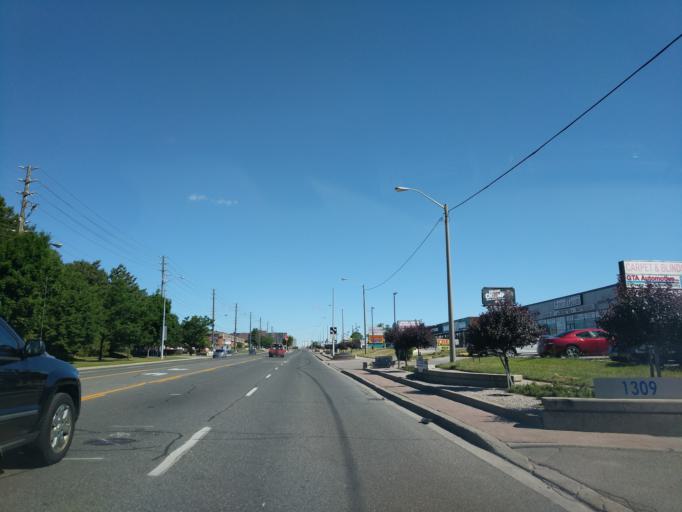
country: CA
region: Ontario
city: Scarborough
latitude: 43.7599
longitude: -79.2788
